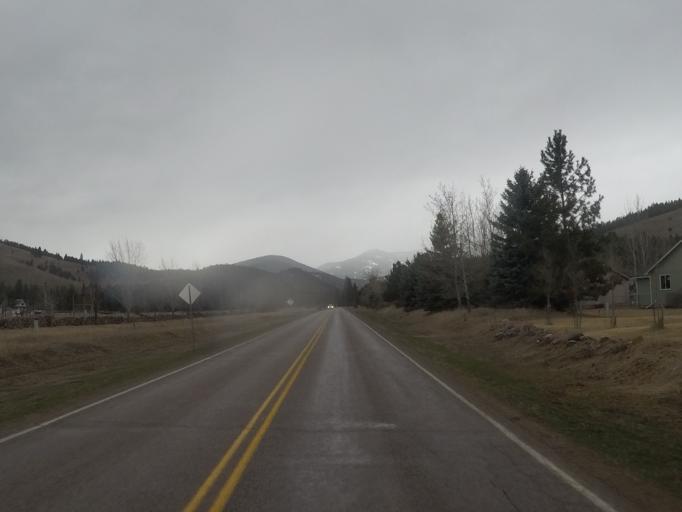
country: US
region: Montana
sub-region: Missoula County
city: East Missoula
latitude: 46.9025
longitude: -113.9604
